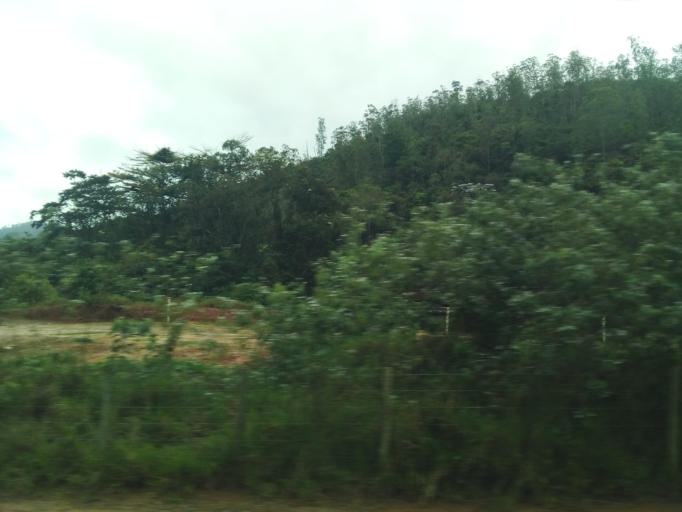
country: BR
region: Minas Gerais
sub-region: Rio Piracicaba
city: Rio Piracicaba
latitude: -19.9463
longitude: -43.1897
